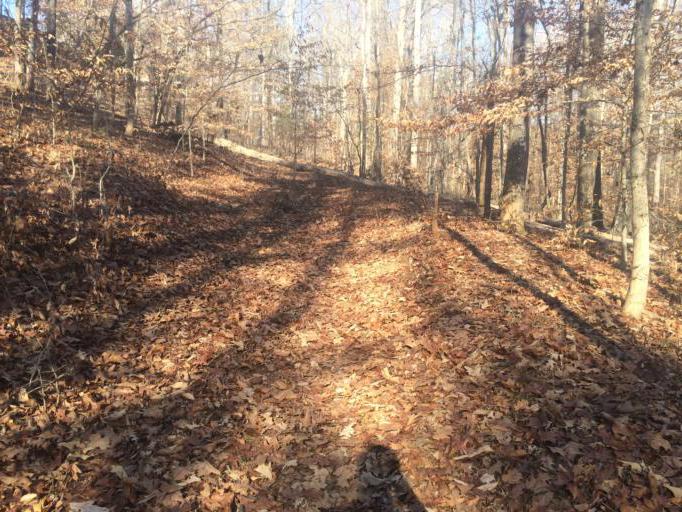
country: US
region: North Carolina
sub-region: Polk County
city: Columbus
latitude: 35.2396
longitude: -82.2164
